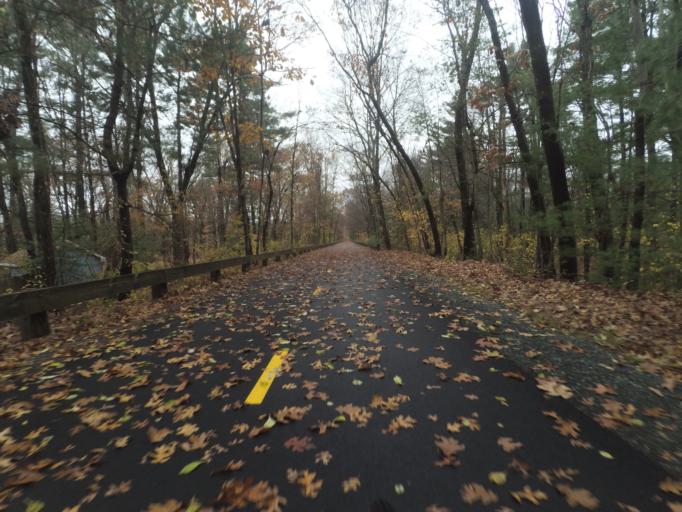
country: US
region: Massachusetts
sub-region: Middlesex County
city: Bedford
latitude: 42.4737
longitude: -71.2610
